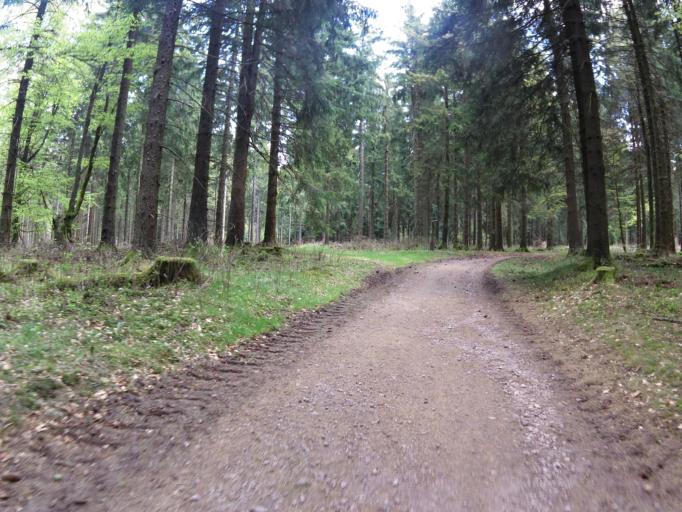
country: DE
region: Thuringia
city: Friedrichroda
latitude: 50.8274
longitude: 10.5370
